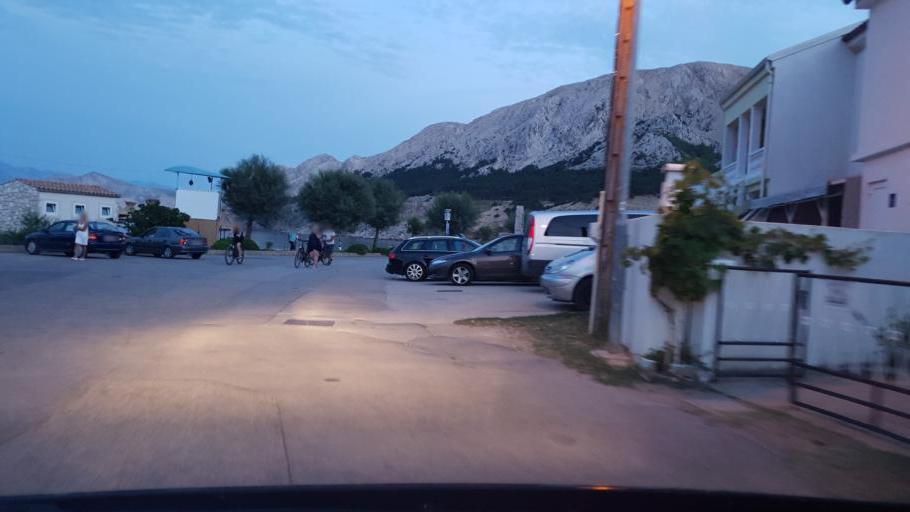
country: HR
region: Primorsko-Goranska
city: Punat
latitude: 44.9621
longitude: 14.7469
